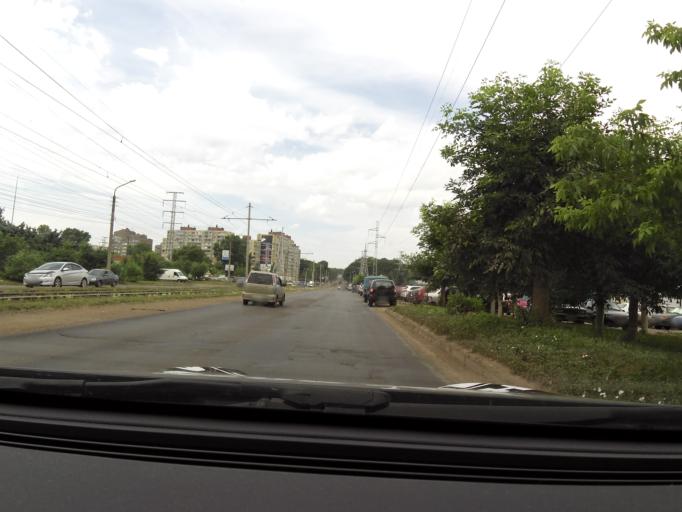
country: RU
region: Bashkortostan
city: Ufa
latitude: 54.7973
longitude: 56.0613
